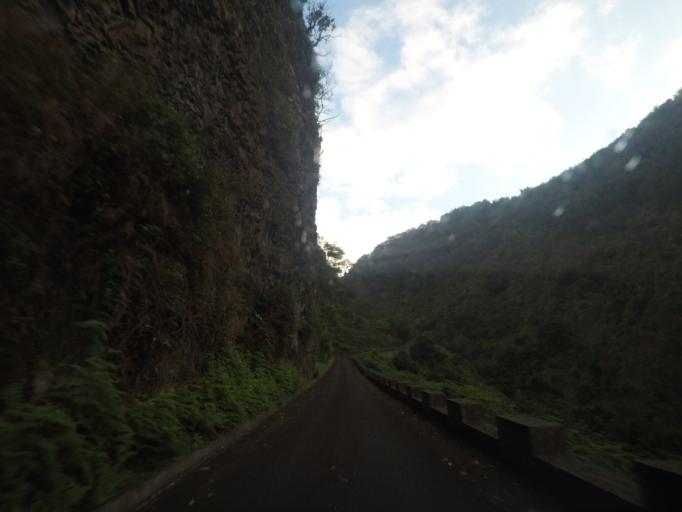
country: PT
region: Madeira
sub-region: Porto Moniz
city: Porto Moniz
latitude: 32.8478
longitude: -17.1625
